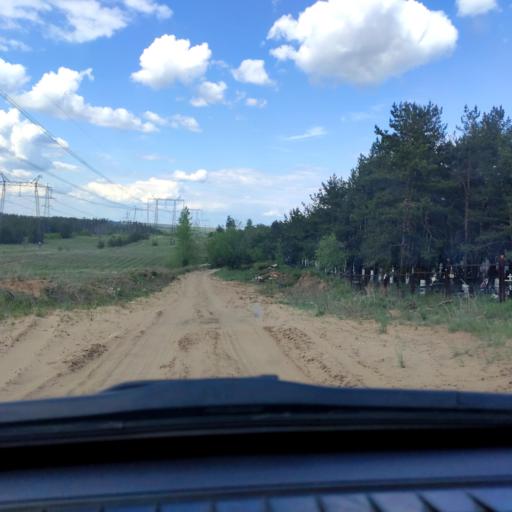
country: RU
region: Samara
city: Zhigulevsk
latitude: 53.5309
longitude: 49.5437
